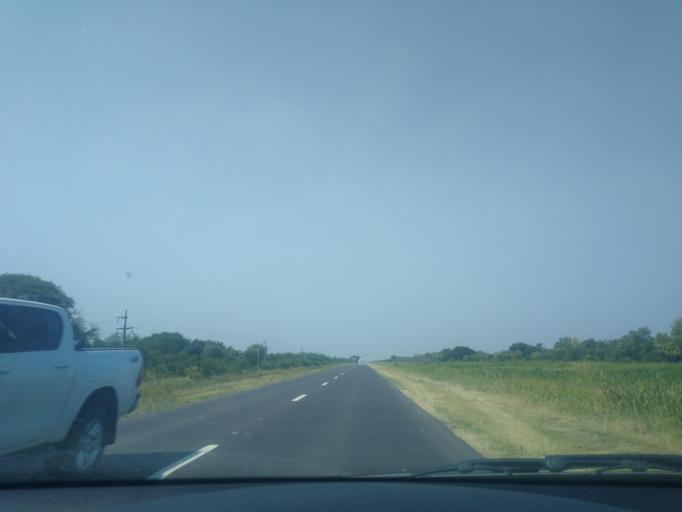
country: AR
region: Chaco
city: Fontana
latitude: -27.5509
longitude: -59.1407
